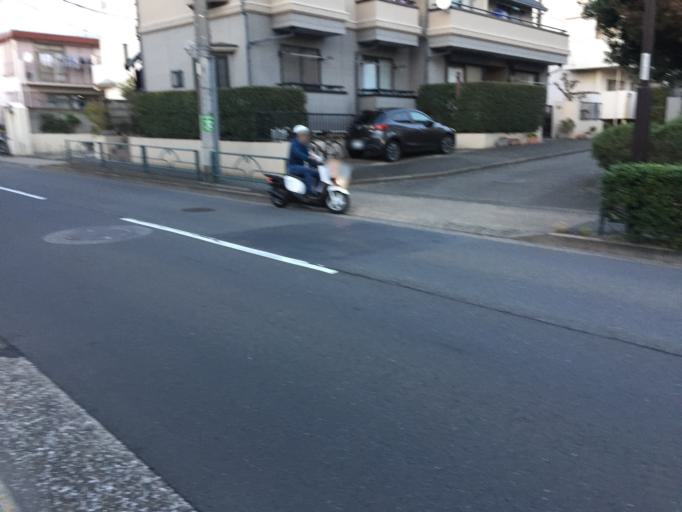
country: JP
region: Tokyo
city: Tokyo
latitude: 35.6365
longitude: 139.6443
